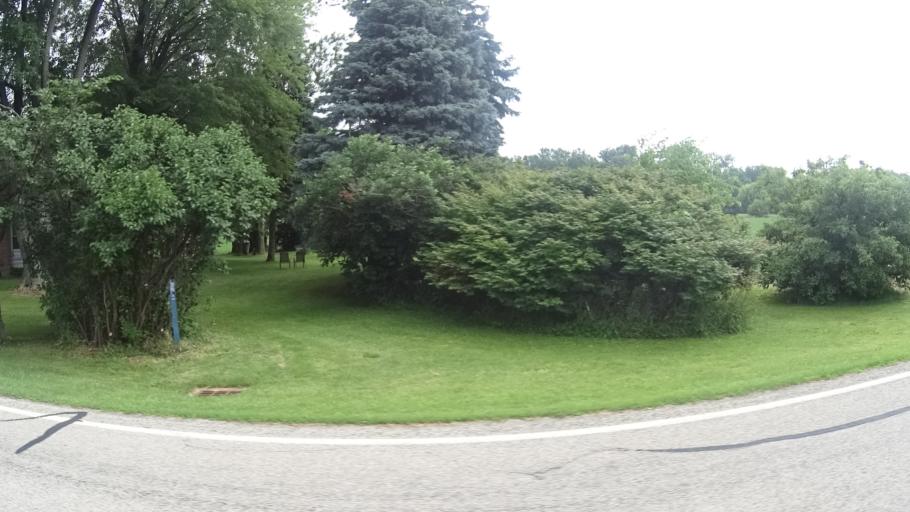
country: US
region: Ohio
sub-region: Huron County
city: Wakeman
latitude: 41.3271
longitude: -82.4534
